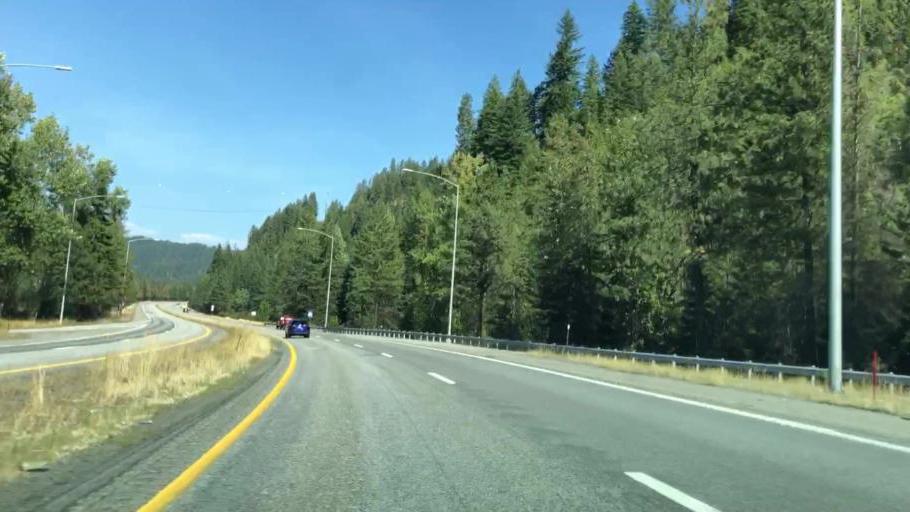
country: US
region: Idaho
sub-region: Shoshone County
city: Pinehurst
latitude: 47.5750
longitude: -116.4396
